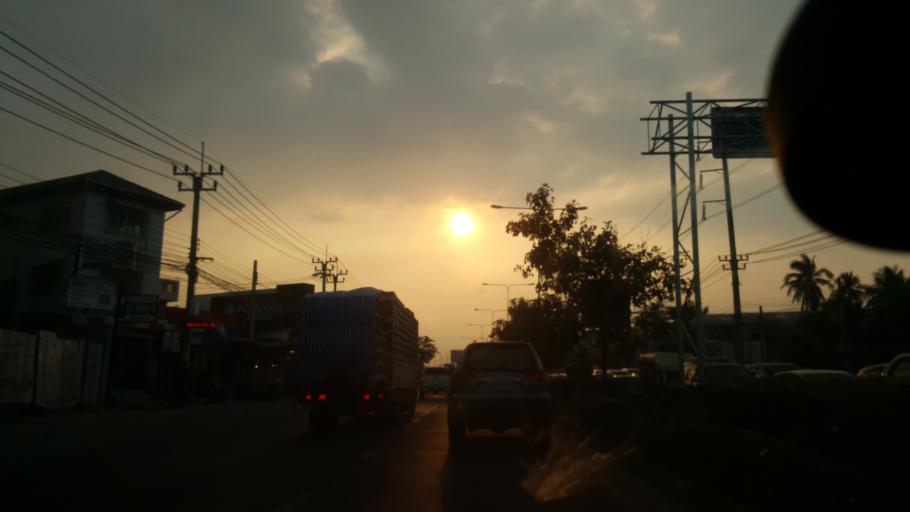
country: TH
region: Bangkok
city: Phasi Charoen
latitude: 13.7103
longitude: 100.4548
